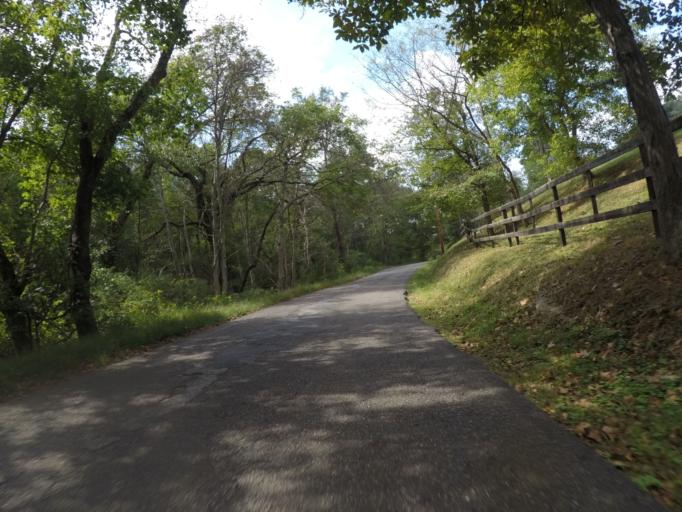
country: US
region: West Virginia
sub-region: Cabell County
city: Huntington
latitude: 38.4506
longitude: -82.4261
